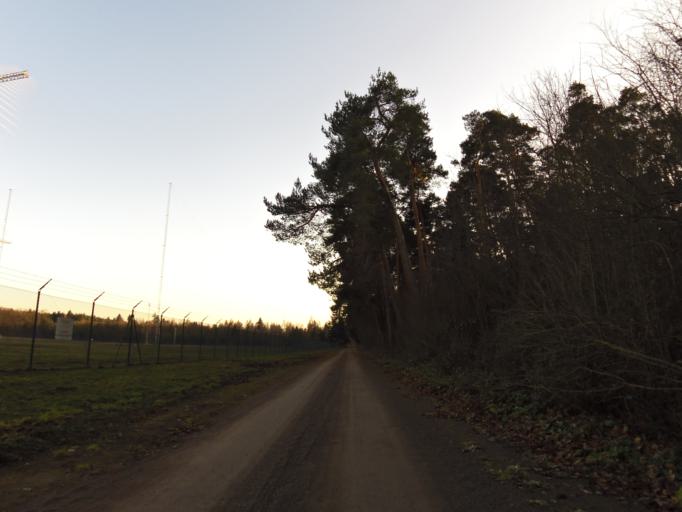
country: DE
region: Hesse
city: Morfelden-Walldorf
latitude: 50.0030
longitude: 8.6092
